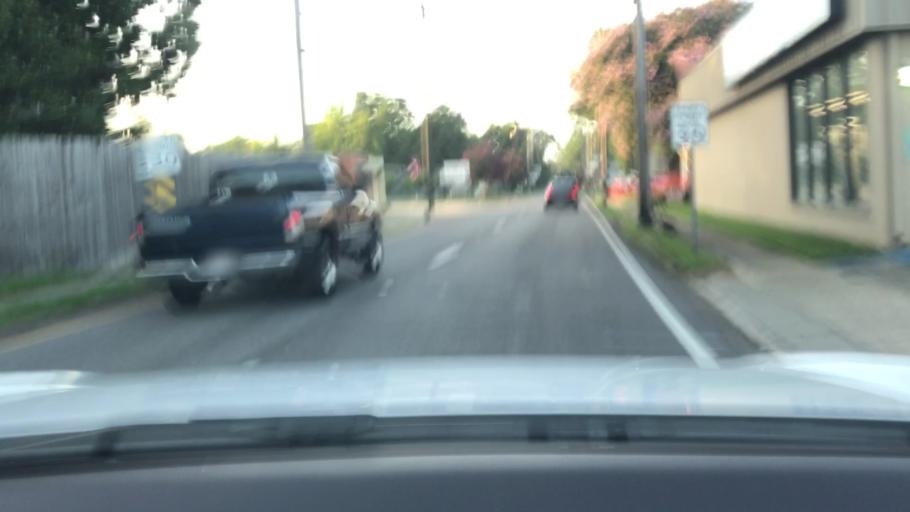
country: US
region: Louisiana
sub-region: Iberville Parish
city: Plaquemine
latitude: 30.2880
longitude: -91.2336
